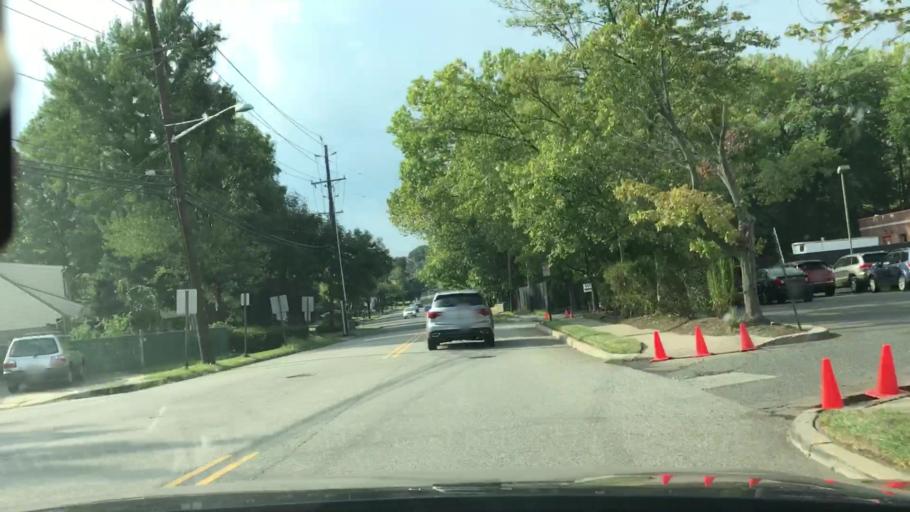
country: US
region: New Jersey
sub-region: Bergen County
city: Rochelle Park
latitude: 40.9165
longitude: -74.0645
